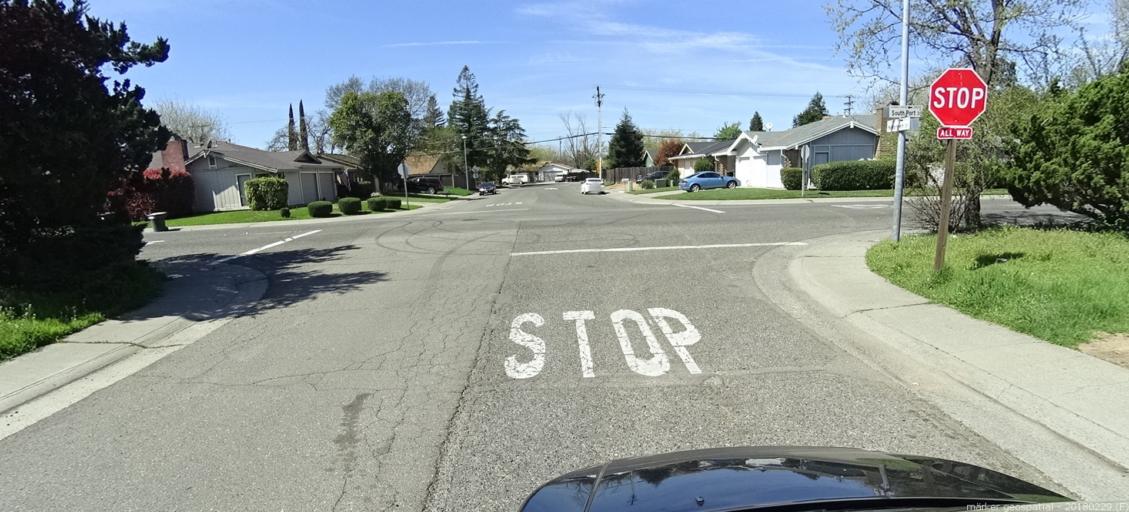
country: US
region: California
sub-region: Sacramento County
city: Rosemont
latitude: 38.5444
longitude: -121.3620
